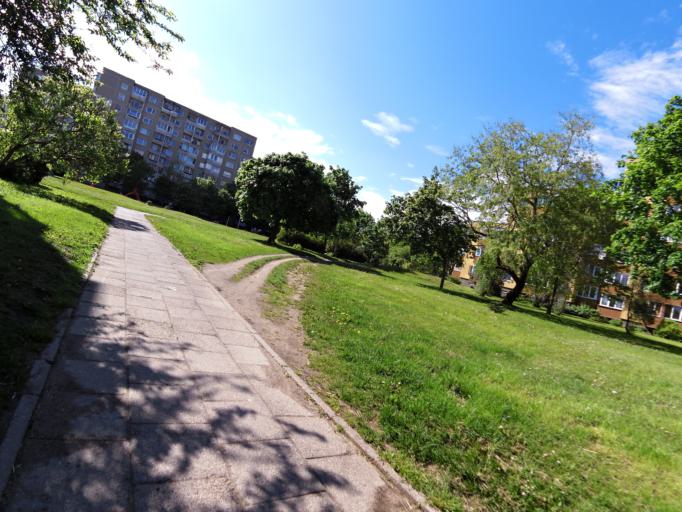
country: LT
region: Vilnius County
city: Seskine
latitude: 54.7225
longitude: 25.2510
